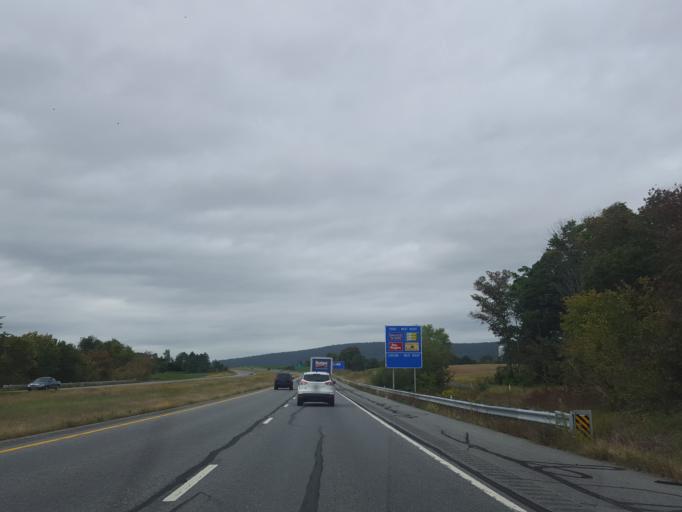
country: US
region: Maryland
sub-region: Frederick County
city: Brunswick
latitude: 39.3515
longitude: -77.6167
